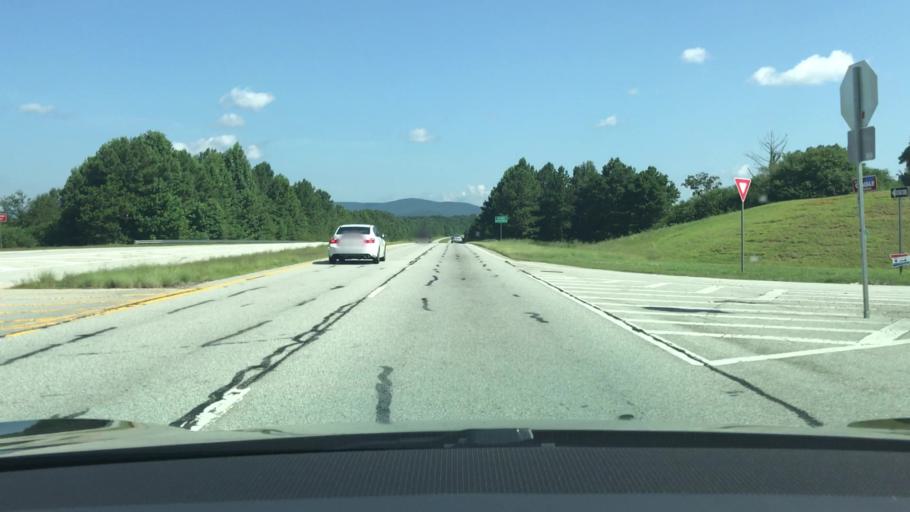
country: US
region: Georgia
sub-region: Habersham County
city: Clarkesville
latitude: 34.6272
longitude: -83.4477
